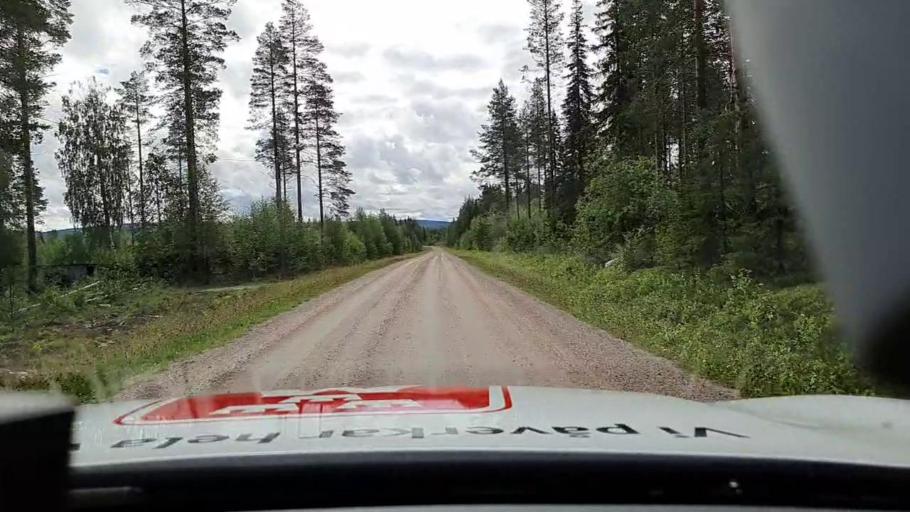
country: SE
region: Norrbotten
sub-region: Overkalix Kommun
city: OEverkalix
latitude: 66.2498
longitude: 23.2064
